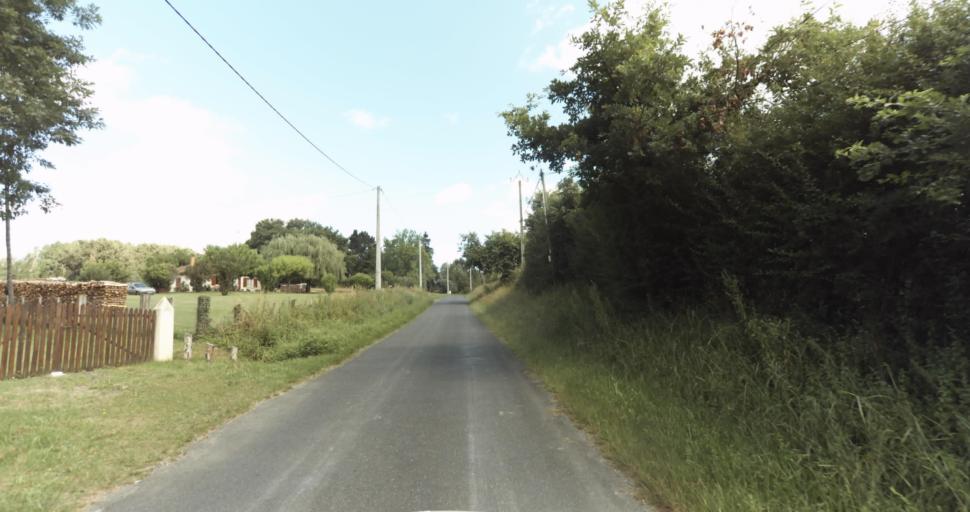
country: FR
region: Aquitaine
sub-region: Departement de la Gironde
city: Bazas
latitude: 44.4457
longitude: -0.2191
